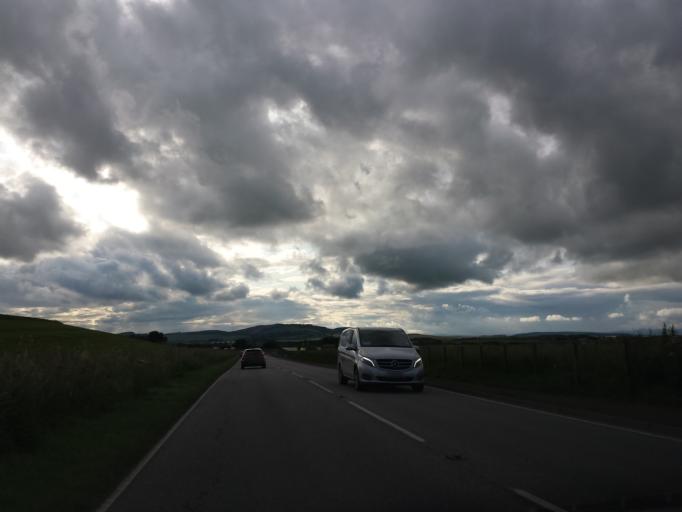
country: GB
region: Scotland
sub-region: Fife
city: Strathkinness
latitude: 56.3576
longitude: -2.8635
